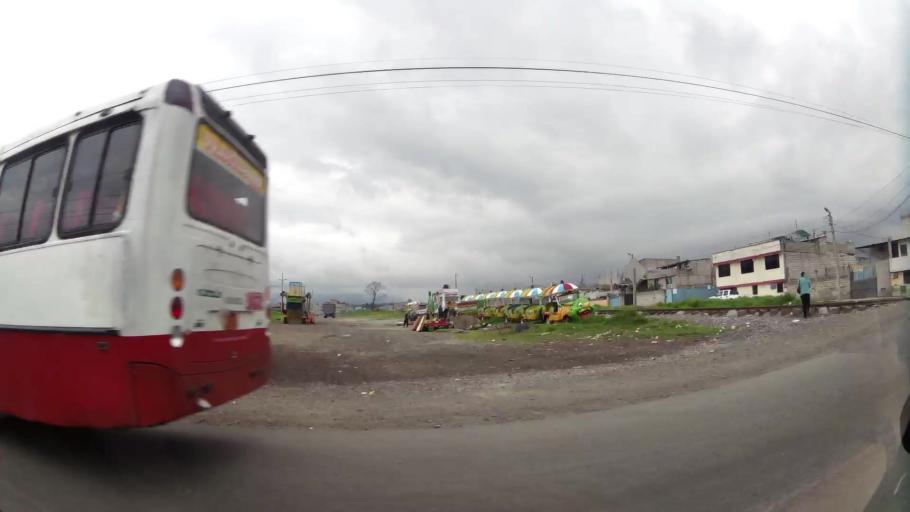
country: EC
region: Pichincha
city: Sangolqui
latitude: -0.3281
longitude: -78.5385
